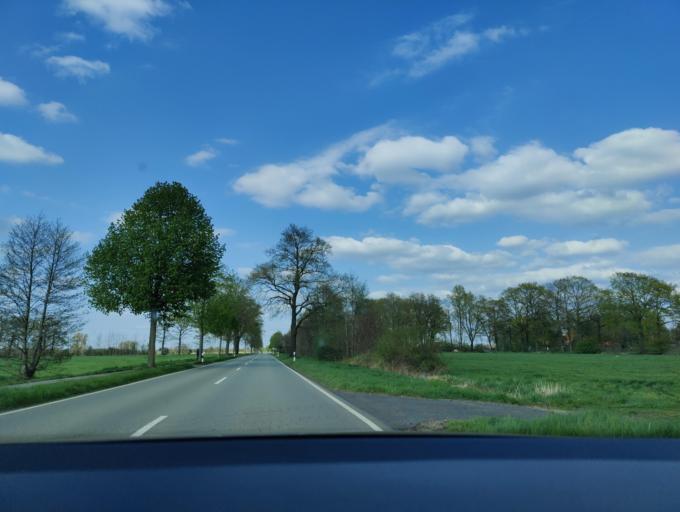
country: DE
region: Lower Saxony
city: Nordhorn
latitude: 52.4676
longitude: 7.1000
